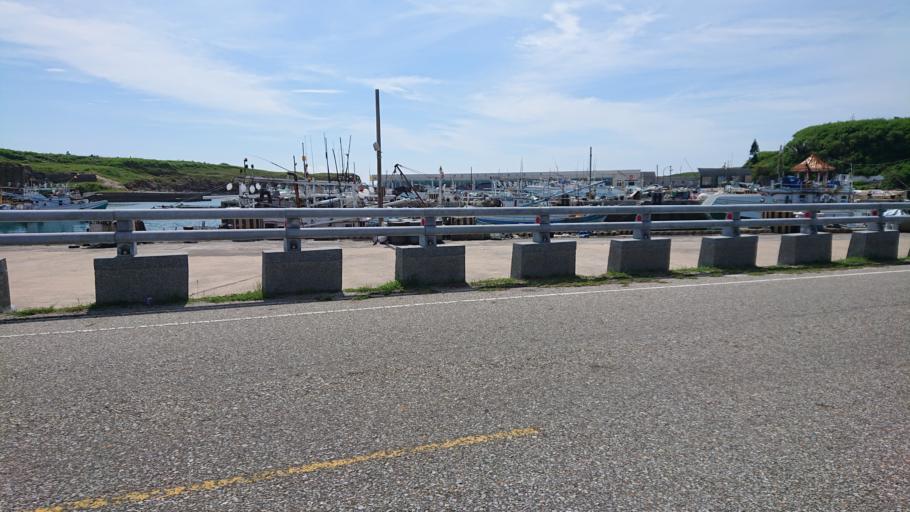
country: TW
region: Taiwan
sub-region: Penghu
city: Ma-kung
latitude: 23.6492
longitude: 119.5197
